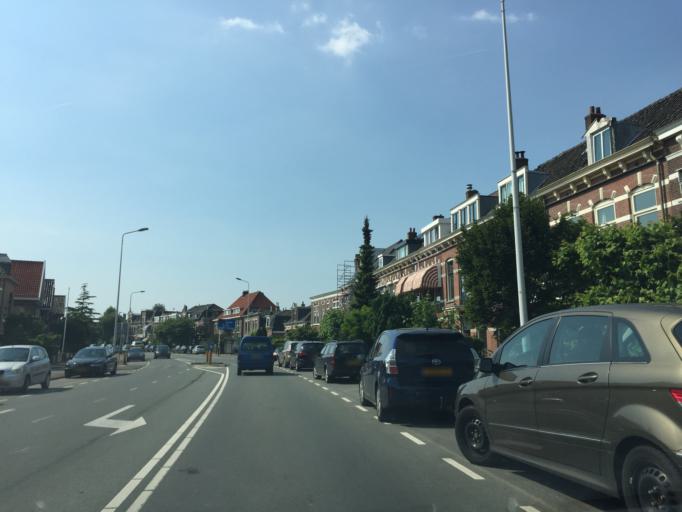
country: NL
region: South Holland
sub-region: Gemeente Leiderdorp
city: Leiderdorp
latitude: 52.1537
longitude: 4.5196
